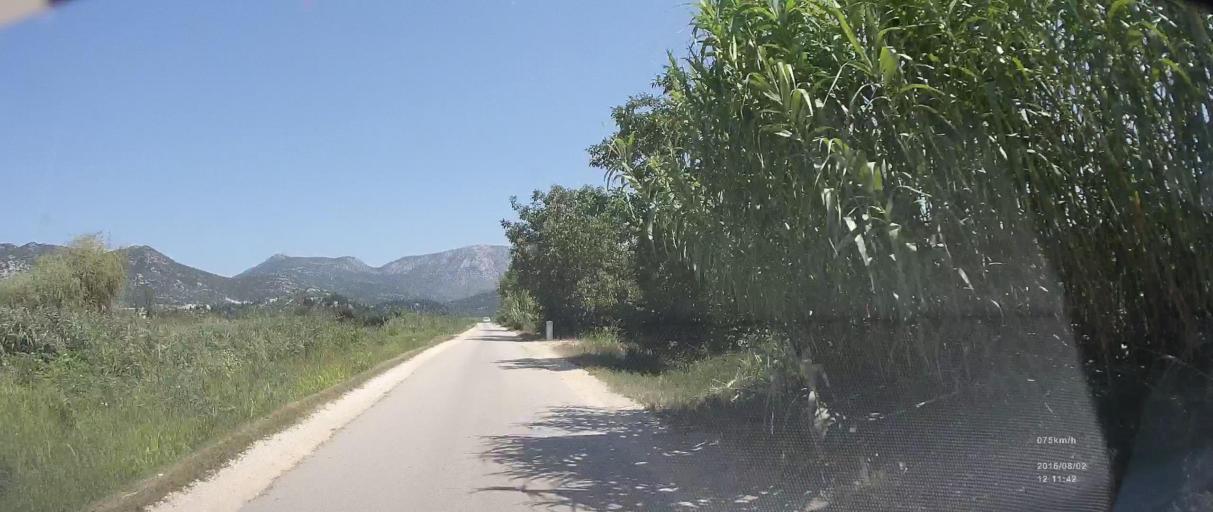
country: HR
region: Dubrovacko-Neretvanska
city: Komin
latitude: 43.0306
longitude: 17.4670
